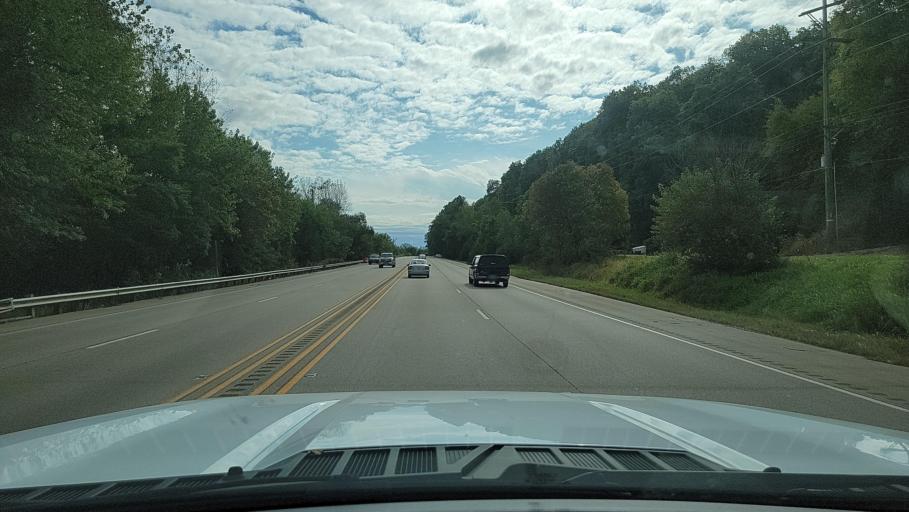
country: US
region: Illinois
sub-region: Peoria County
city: Bartonville
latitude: 40.6171
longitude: -89.6576
